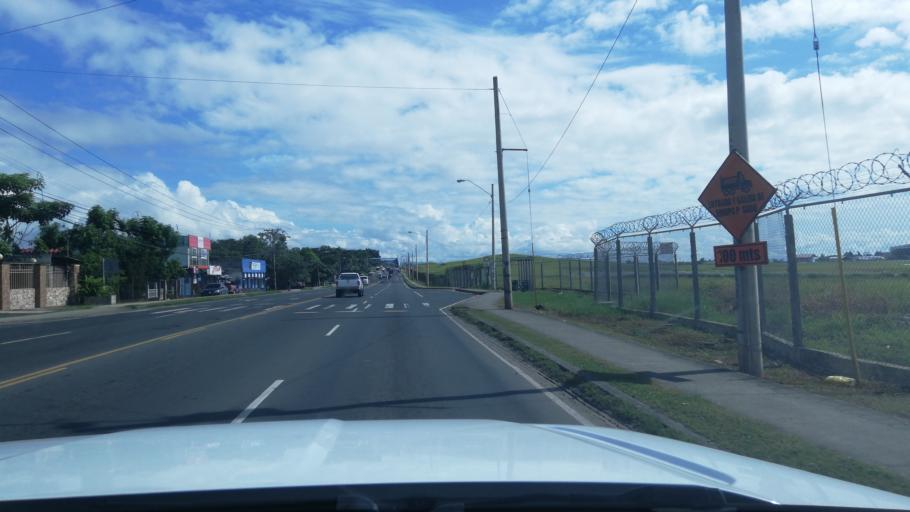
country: PA
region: Panama
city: Tocumen
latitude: 9.0884
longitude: -79.3823
